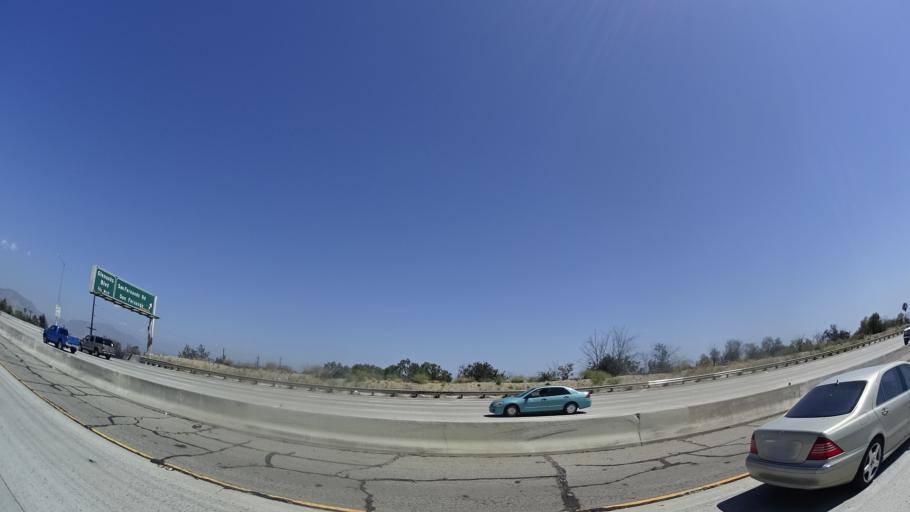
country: US
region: California
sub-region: Los Angeles County
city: San Fernando
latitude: 34.2697
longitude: -118.4328
